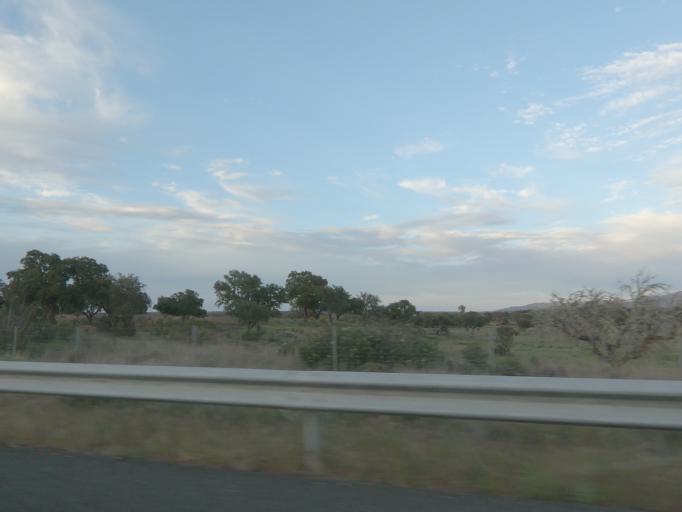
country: ES
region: Extremadura
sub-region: Provincia de Caceres
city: Casas de Don Antonio
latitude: 39.2022
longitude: -6.2818
